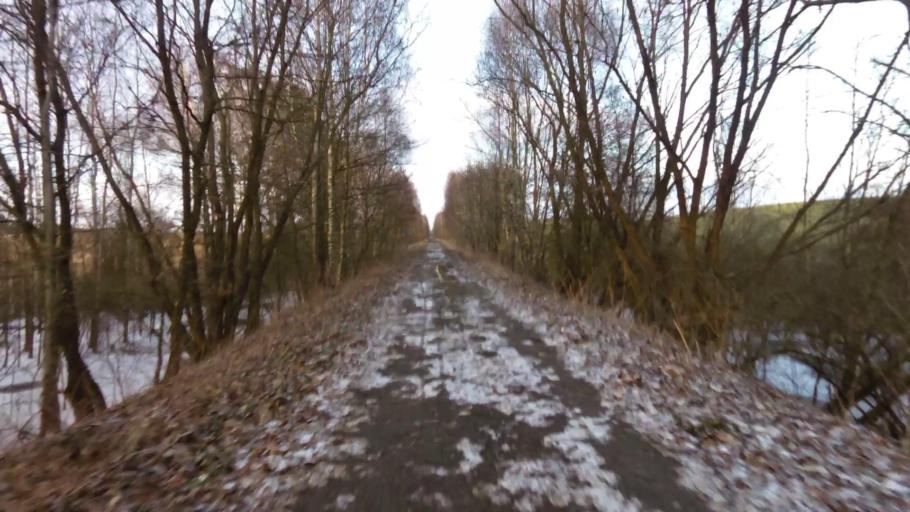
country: PL
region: West Pomeranian Voivodeship
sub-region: Powiat drawski
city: Zlocieniec
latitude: 53.6093
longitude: 16.0495
